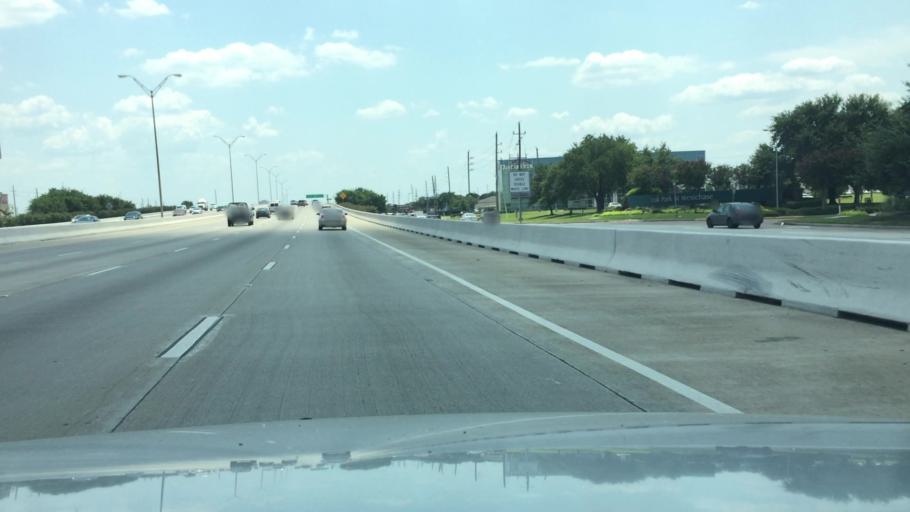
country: US
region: Texas
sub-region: Harris County
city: Bunker Hill Village
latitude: 29.7089
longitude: -95.5577
